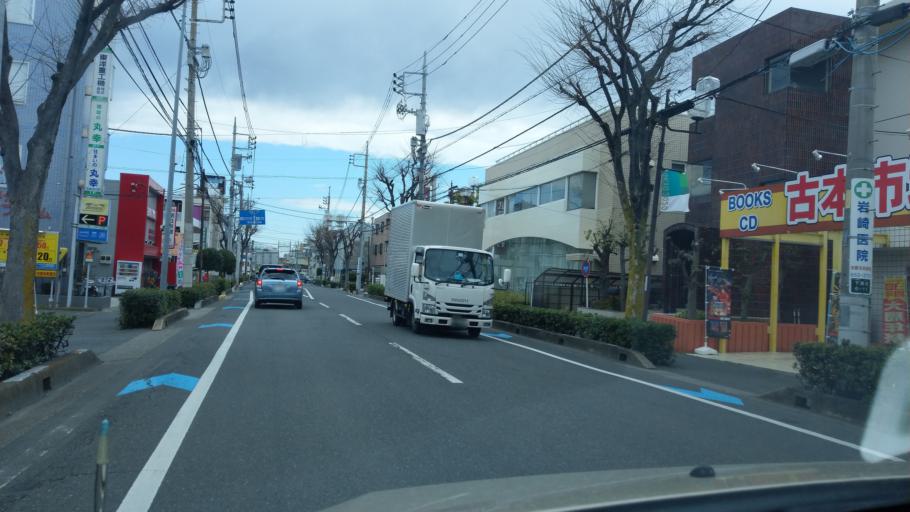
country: JP
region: Saitama
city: Yono
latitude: 35.8821
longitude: 139.6276
